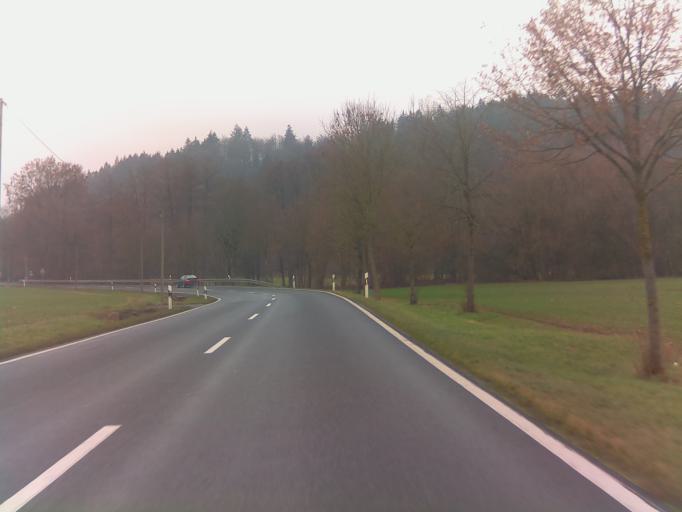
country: DE
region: Thuringia
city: Ahlstadt
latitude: 50.4902
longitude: 10.6998
